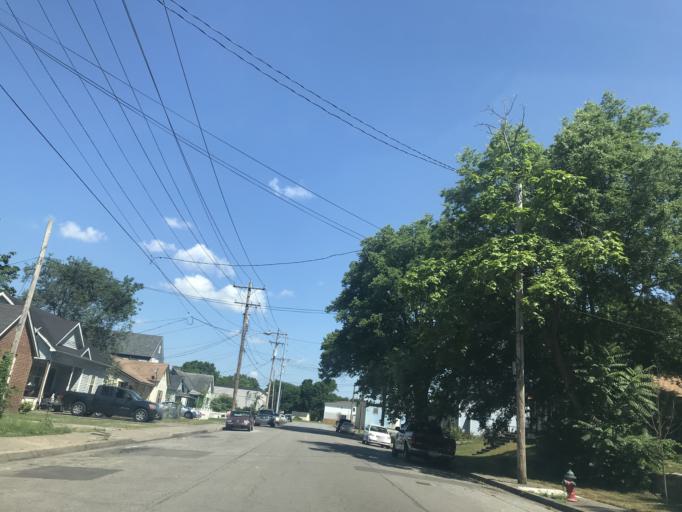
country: US
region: Tennessee
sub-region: Davidson County
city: Nashville
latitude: 36.1789
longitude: -86.8068
